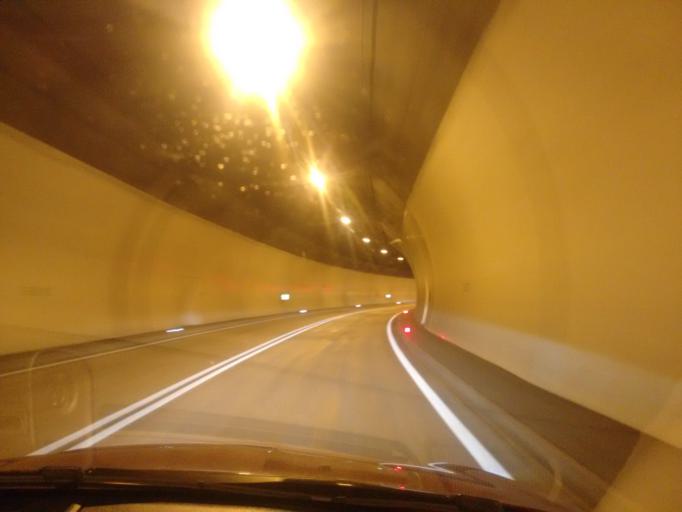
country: AT
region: Upper Austria
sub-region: Politischer Bezirk Gmunden
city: Ebensee
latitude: 47.8479
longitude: 13.7788
